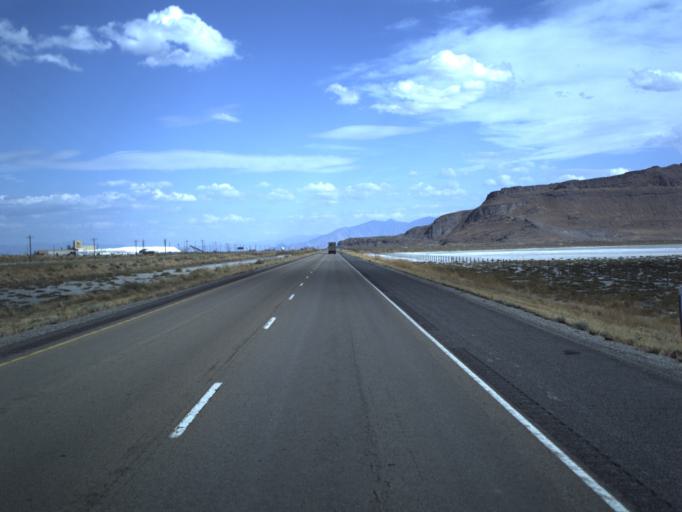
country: US
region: Utah
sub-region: Tooele County
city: Grantsville
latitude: 40.7481
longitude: -112.6779
